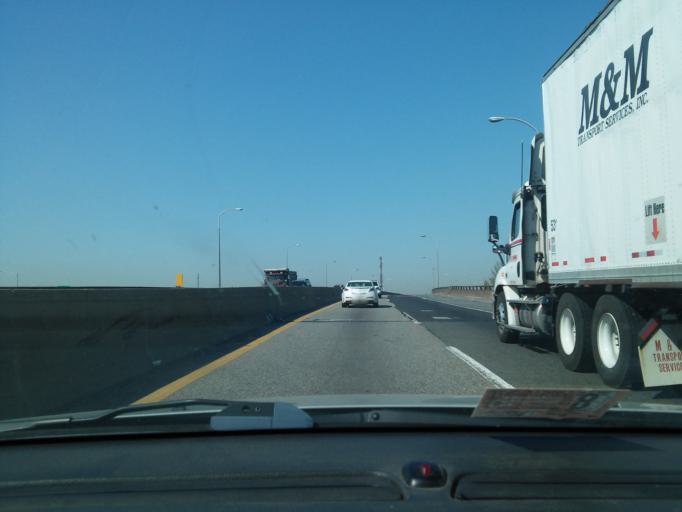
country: US
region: New Jersey
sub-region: Hudson County
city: Bayonne
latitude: 40.6871
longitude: -74.0902
